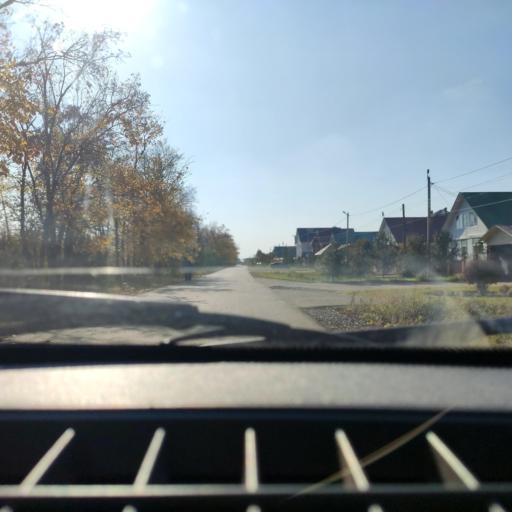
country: RU
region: Bashkortostan
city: Ufa
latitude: 54.6298
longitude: 55.9189
